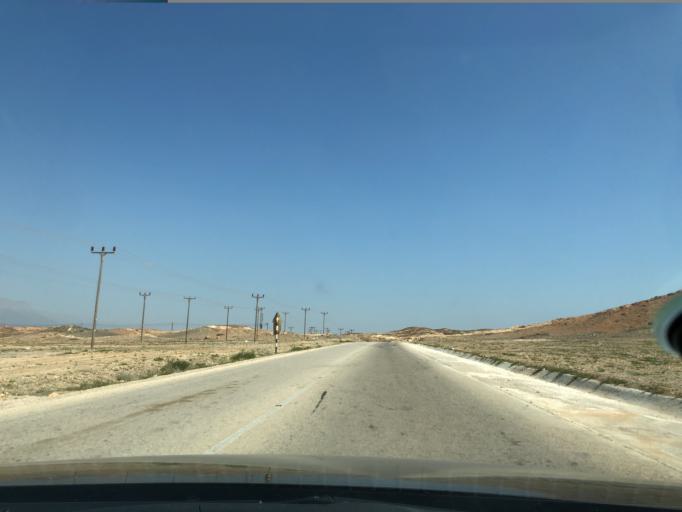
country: OM
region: Zufar
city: Salalah
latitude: 17.0032
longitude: 54.7443
